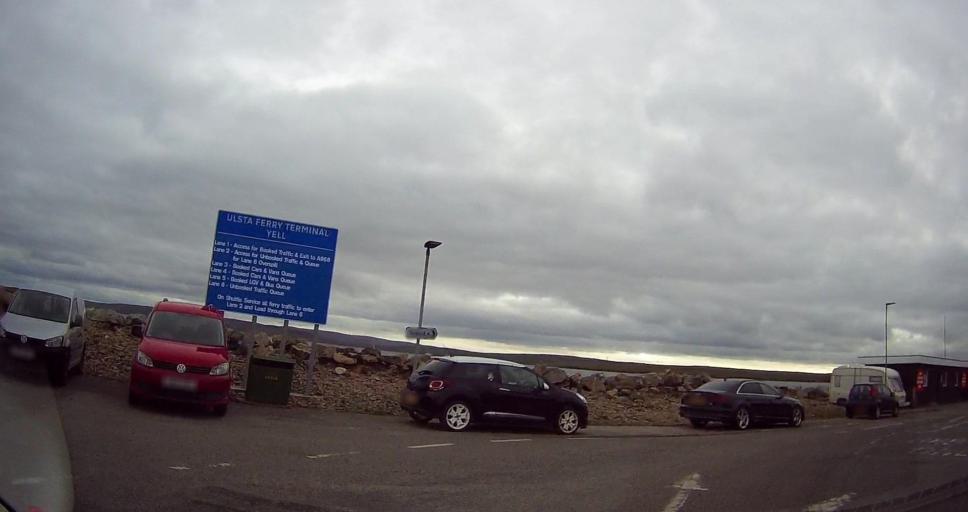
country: GB
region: Scotland
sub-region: Shetland Islands
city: Shetland
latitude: 60.4964
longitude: -1.1592
